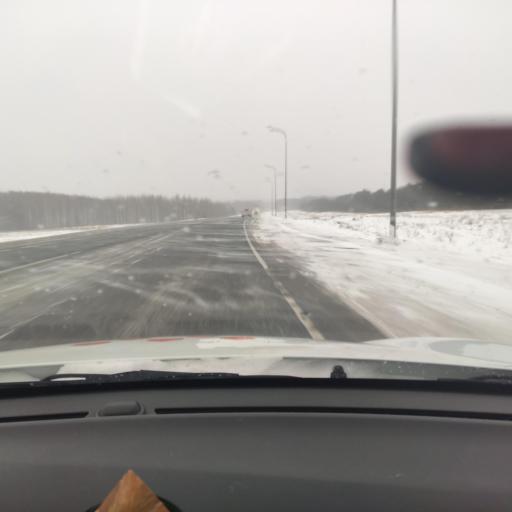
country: RU
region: Tatarstan
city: Verkhniy Uslon
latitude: 55.7042
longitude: 48.8897
